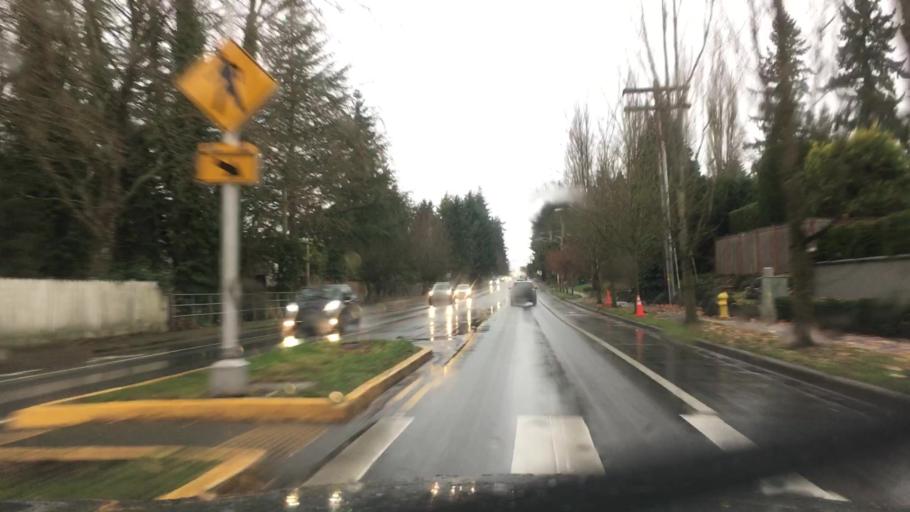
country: US
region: Washington
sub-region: King County
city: Kingsgate
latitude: 47.7041
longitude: -122.1903
